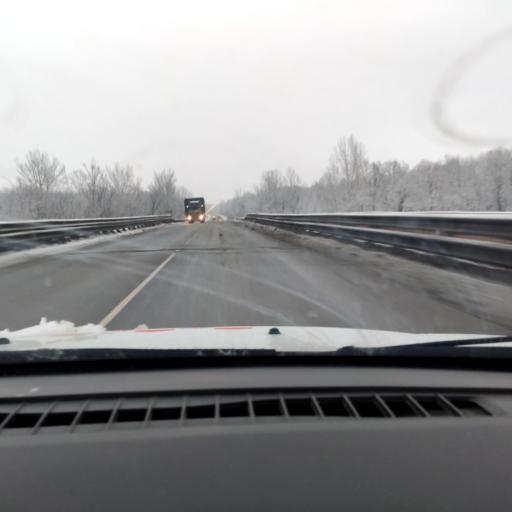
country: RU
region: Bashkortostan
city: Urman
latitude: 54.8271
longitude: 56.9029
